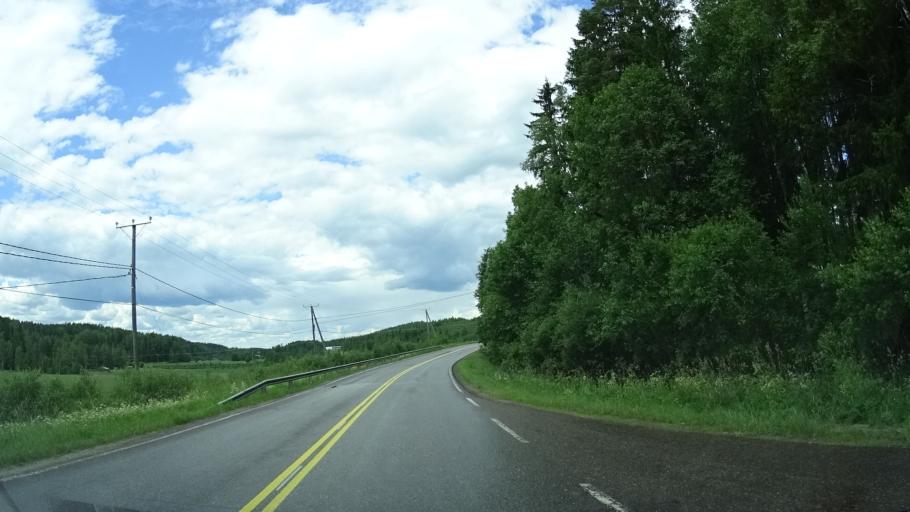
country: FI
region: Uusimaa
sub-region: Helsinki
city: Espoo
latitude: 60.3597
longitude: 24.6400
